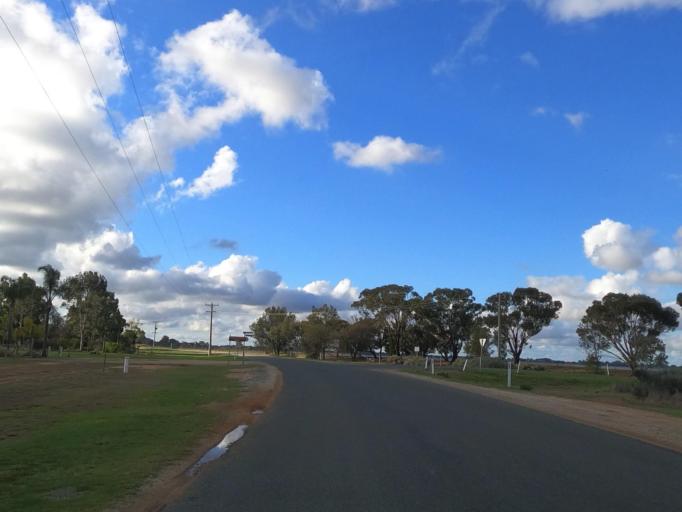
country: AU
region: Victoria
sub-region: Swan Hill
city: Swan Hill
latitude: -35.4481
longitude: 143.6265
